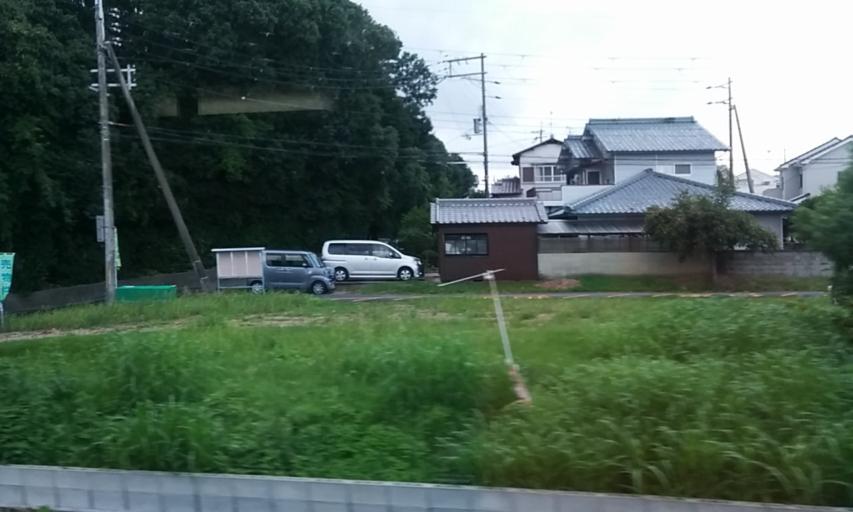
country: JP
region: Nara
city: Nara-shi
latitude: 34.6728
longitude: 135.7832
